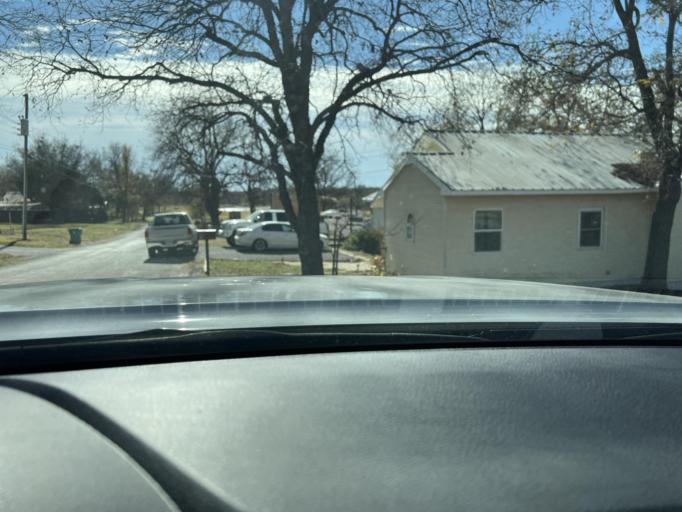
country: US
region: Texas
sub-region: Eastland County
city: Eastland
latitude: 32.3890
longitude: -98.8210
